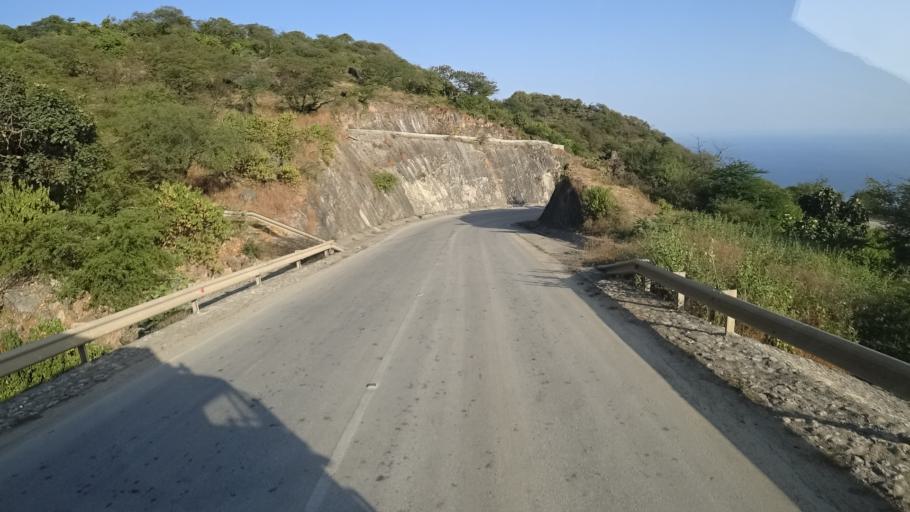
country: OM
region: Zufar
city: Salalah
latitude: 17.0596
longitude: 54.6119
